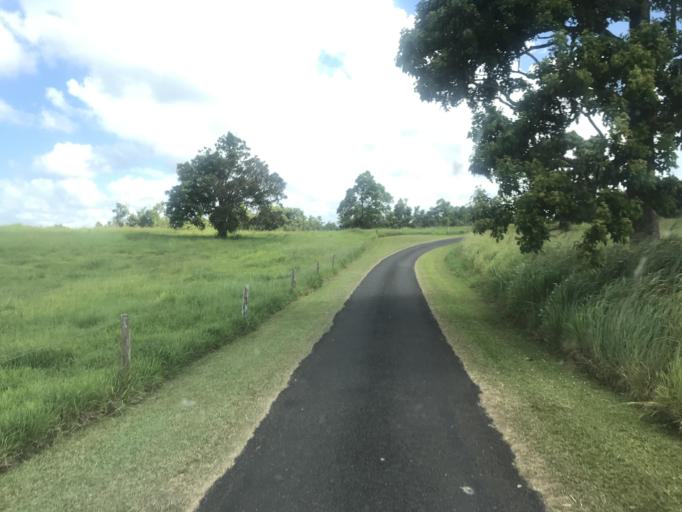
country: AU
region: Queensland
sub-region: Tablelands
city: Ravenshoe
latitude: -17.5564
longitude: 145.6904
